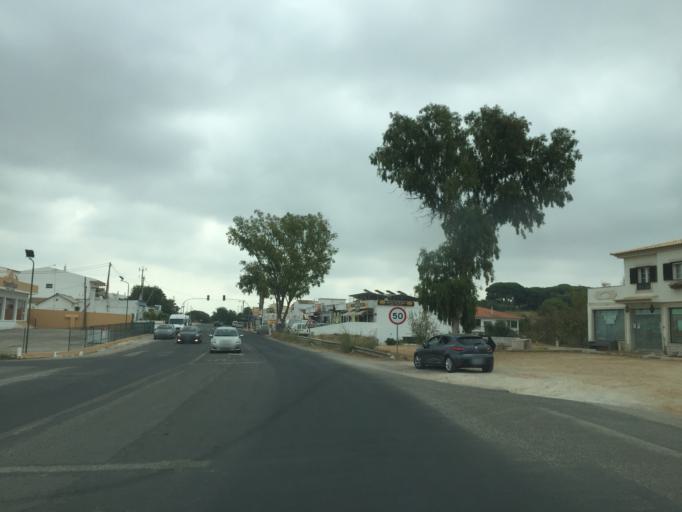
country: PT
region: Faro
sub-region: Faro
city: Santa Barbara de Nexe
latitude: 37.0771
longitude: -7.9884
